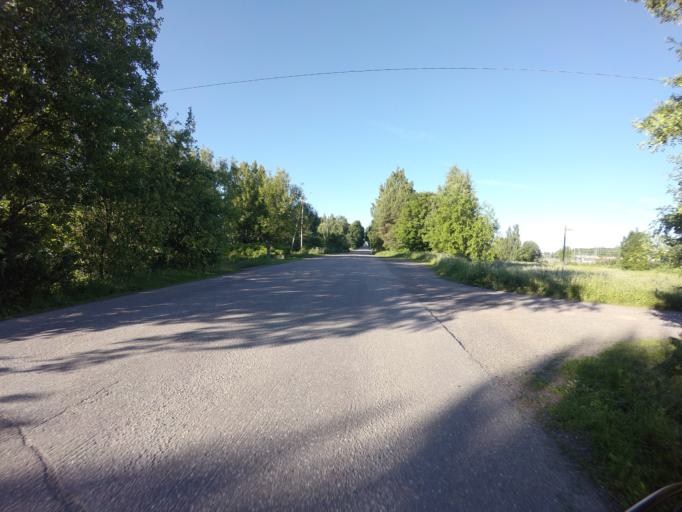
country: FI
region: Varsinais-Suomi
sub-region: Turku
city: Turku
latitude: 60.4761
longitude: 22.2946
